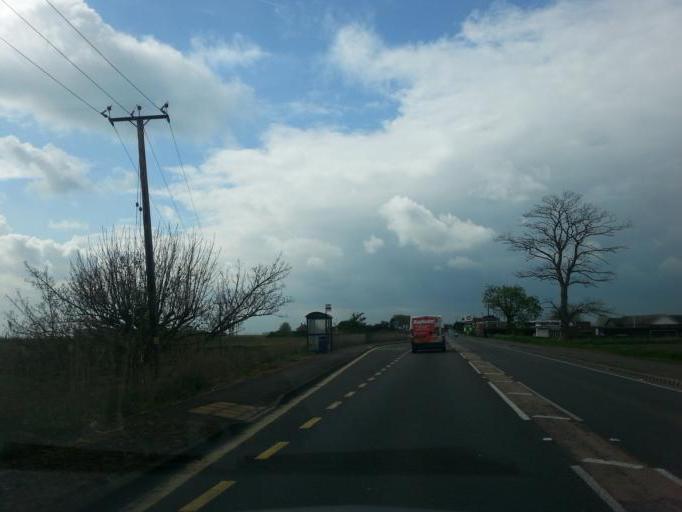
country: GB
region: England
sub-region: Peterborough
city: Thorney
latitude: 52.6163
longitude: -0.0155
